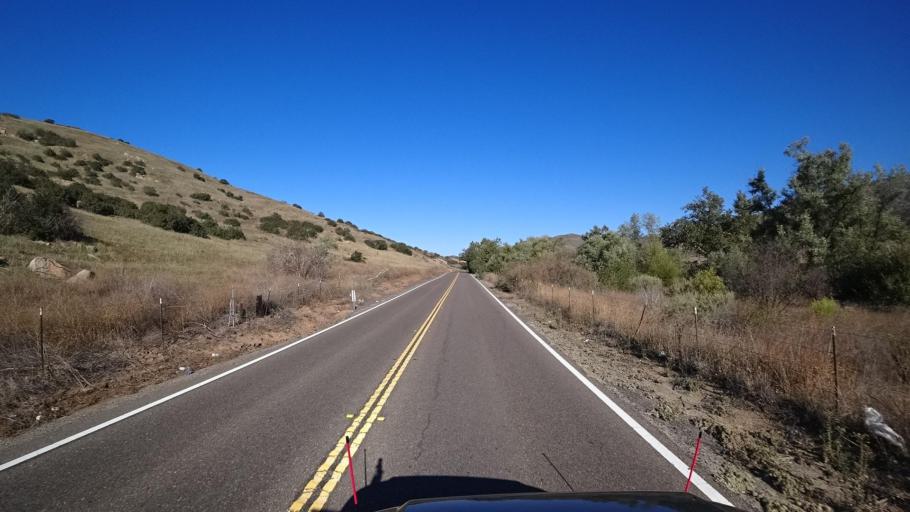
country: US
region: California
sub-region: San Diego County
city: Jamul
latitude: 32.6594
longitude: -116.8101
